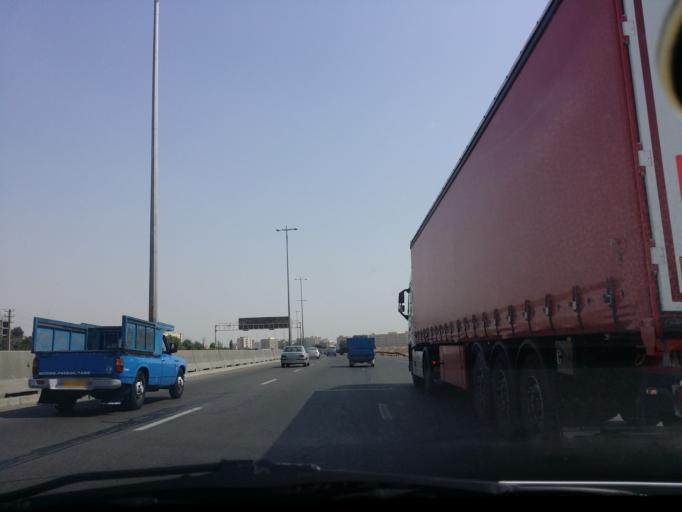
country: IR
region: Alborz
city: Karaj
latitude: 35.8336
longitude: 50.9101
